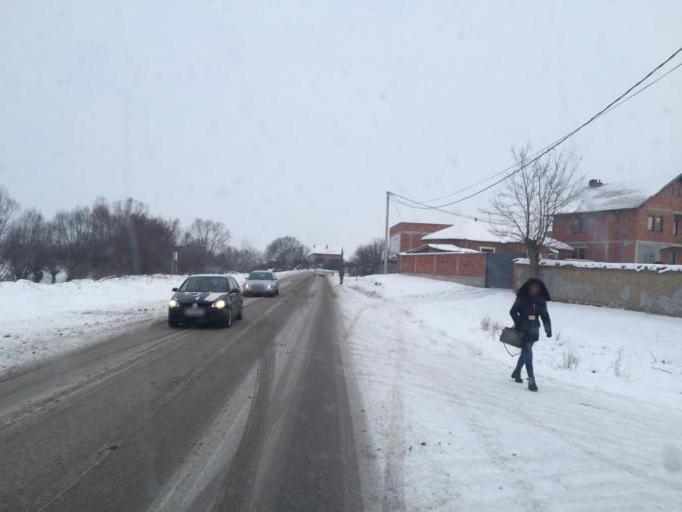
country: XK
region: Pristina
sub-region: Komuna e Drenasit
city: Glogovac
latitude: 42.5906
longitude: 20.8930
